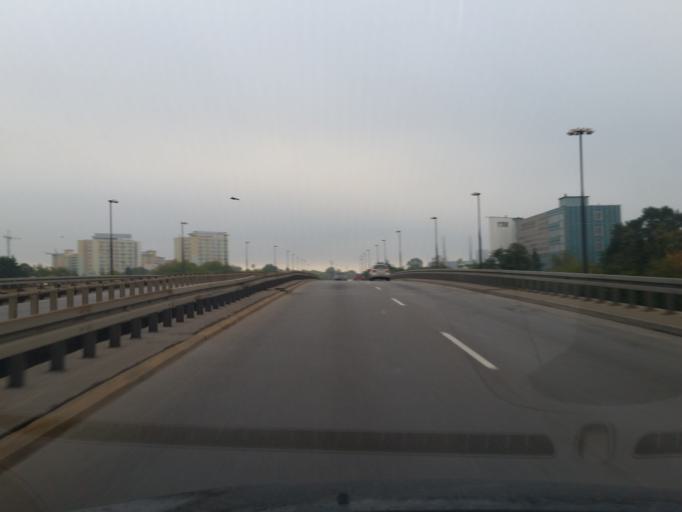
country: PL
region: Masovian Voivodeship
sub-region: Warszawa
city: Bialoleka
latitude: 52.3085
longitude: 20.9827
